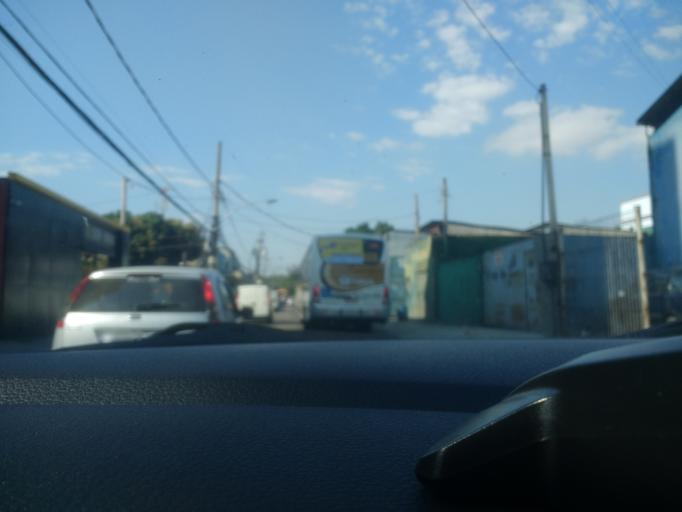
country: BR
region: Rio de Janeiro
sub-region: Duque De Caxias
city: Duque de Caxias
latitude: -22.7991
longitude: -43.2942
